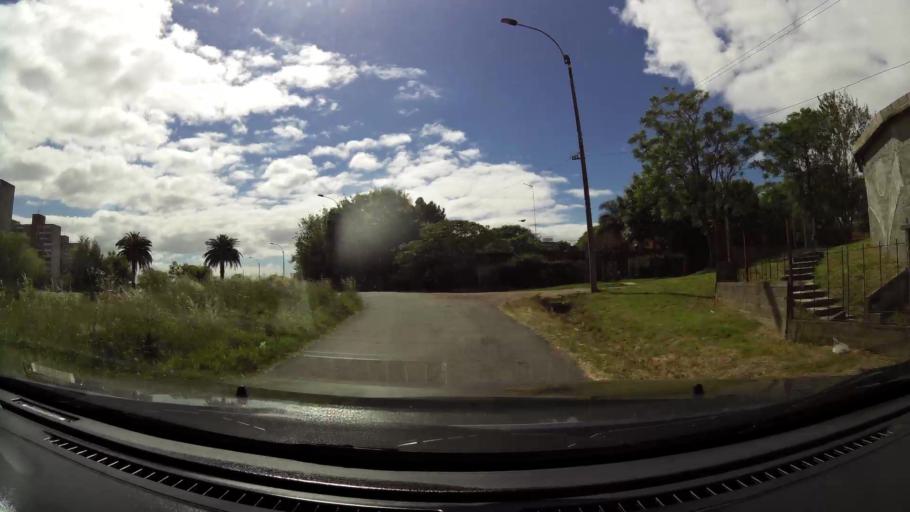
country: UY
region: Canelones
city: Paso de Carrasco
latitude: -34.8847
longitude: -56.1146
